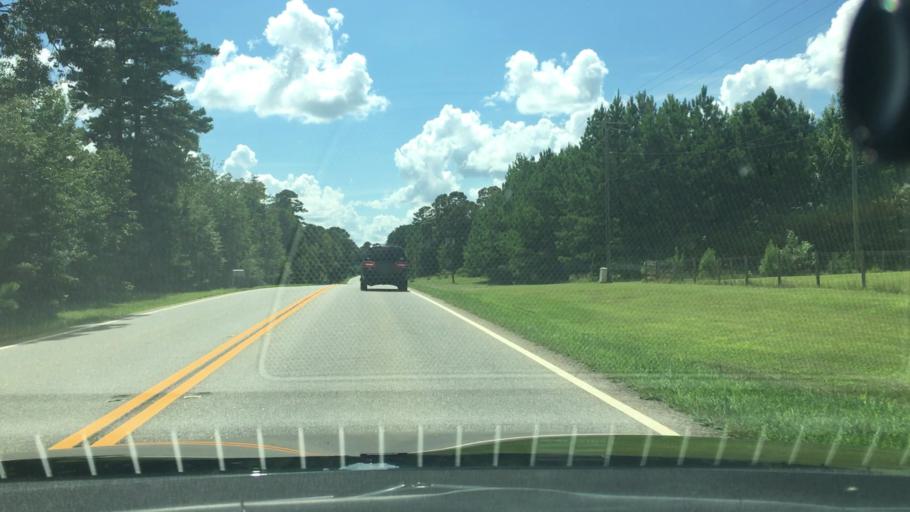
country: US
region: Georgia
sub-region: Putnam County
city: Eatonton
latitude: 33.3081
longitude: -83.4741
